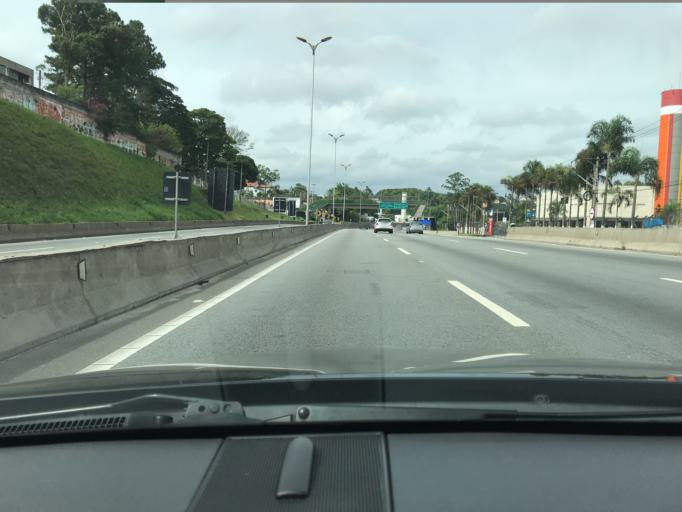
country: BR
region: Sao Paulo
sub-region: Taboao Da Serra
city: Taboao da Serra
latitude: -23.5897
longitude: -46.8168
